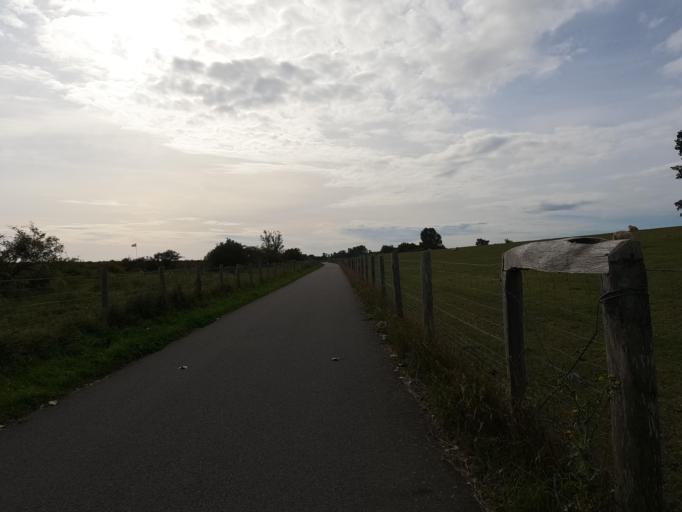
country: DE
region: Schleswig-Holstein
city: Dahme
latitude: 54.2475
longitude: 11.0804
